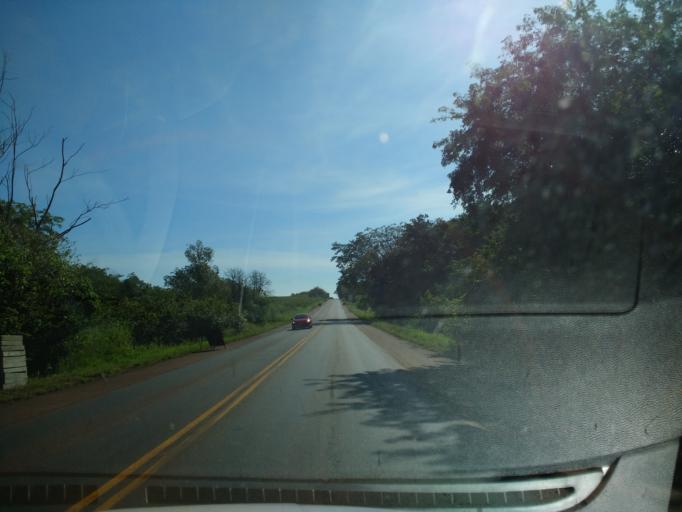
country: BR
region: Parana
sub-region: Alto Piquiri
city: Alto Piquiri
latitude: -24.2420
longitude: -53.5421
